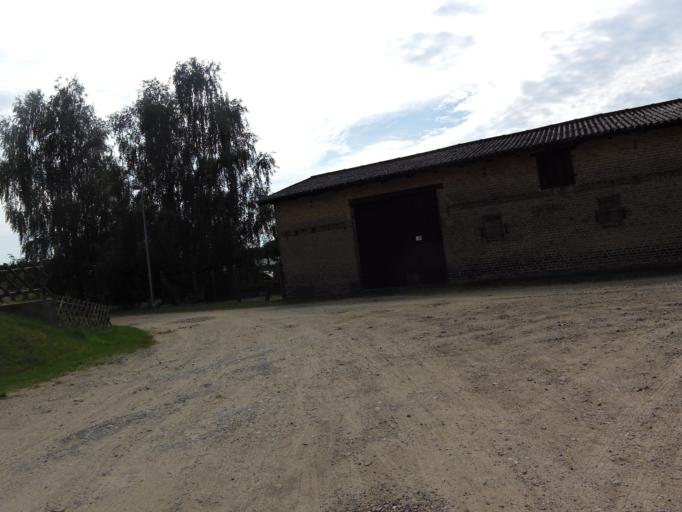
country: DE
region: Brandenburg
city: Lychen
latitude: 53.2829
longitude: 13.3026
